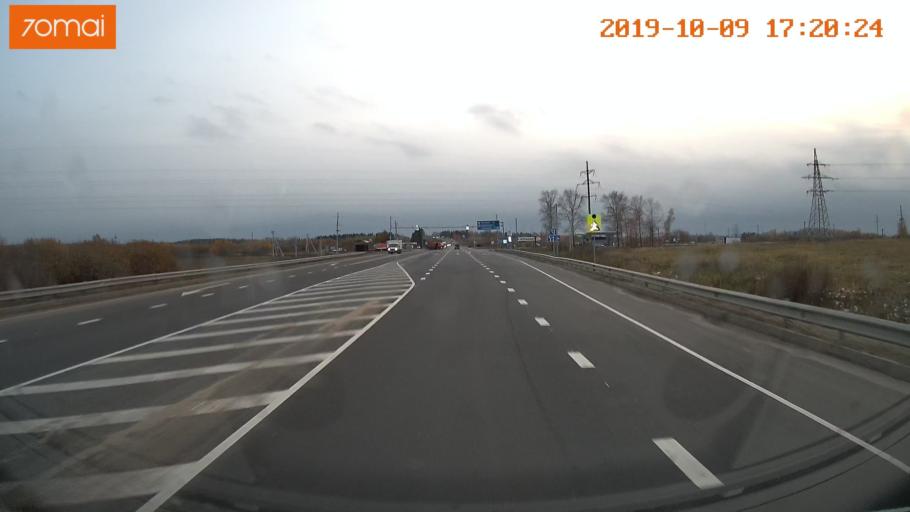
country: RU
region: Ivanovo
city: Furmanov
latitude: 57.2350
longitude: 41.1418
